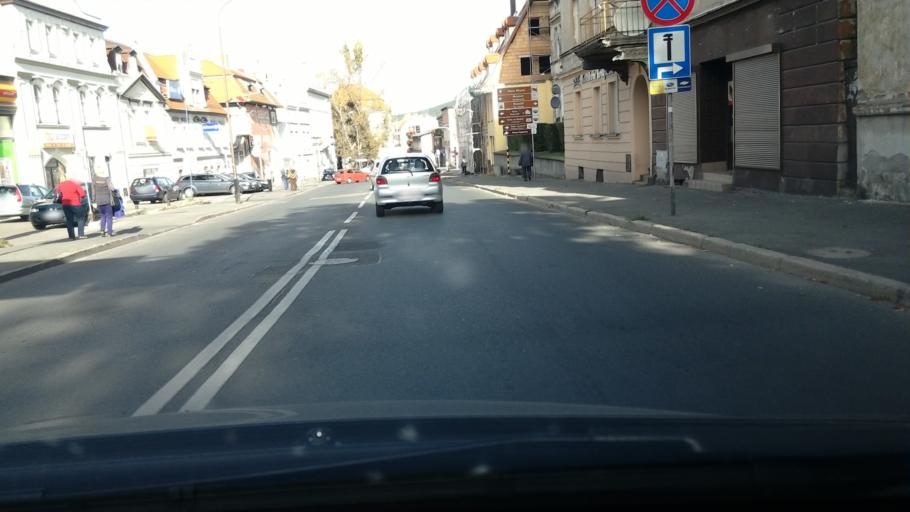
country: PL
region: Lower Silesian Voivodeship
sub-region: Jelenia Gora
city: Jelenia Gora
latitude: 50.8986
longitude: 15.7411
